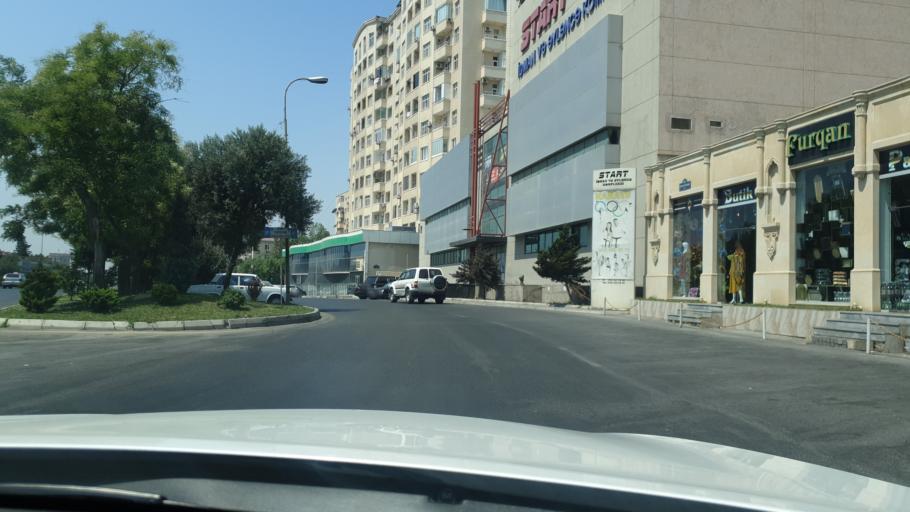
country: AZ
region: Baki
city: Bakixanov
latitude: 40.4137
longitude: 49.9511
